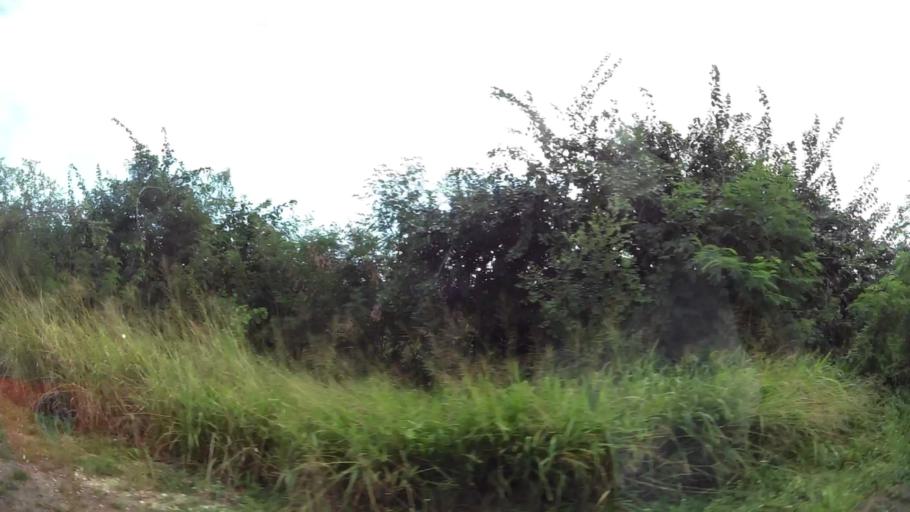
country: AG
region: Saint Paul
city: Liberta
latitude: 17.0507
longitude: -61.7494
